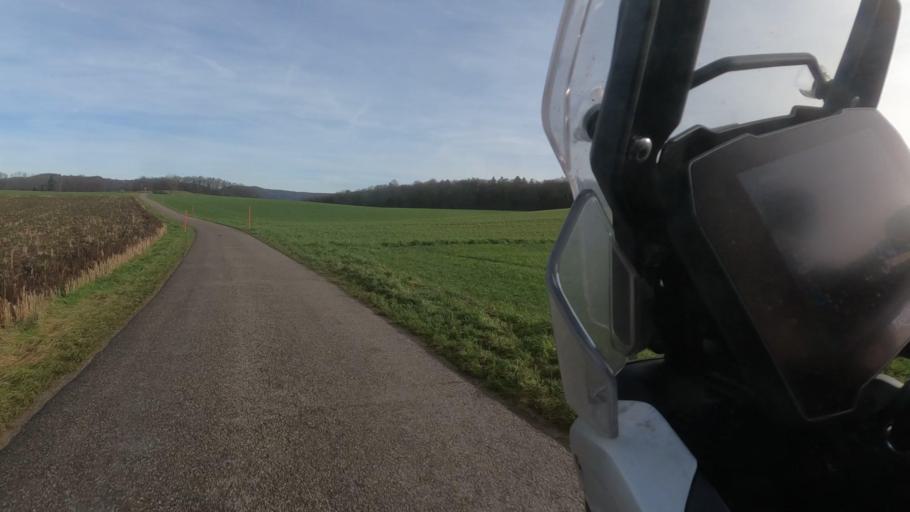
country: CH
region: Zurich
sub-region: Bezirk Buelach
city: Glattfelden
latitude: 47.5435
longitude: 8.5049
